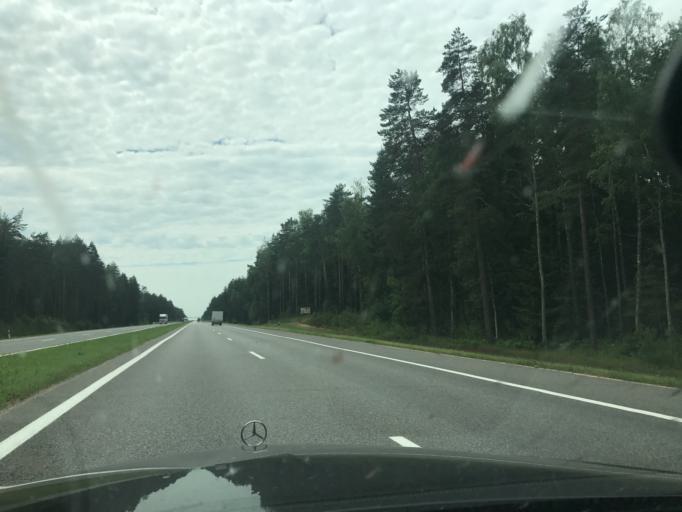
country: BY
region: Minsk
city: Slabada
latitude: 53.9127
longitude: 27.9513
